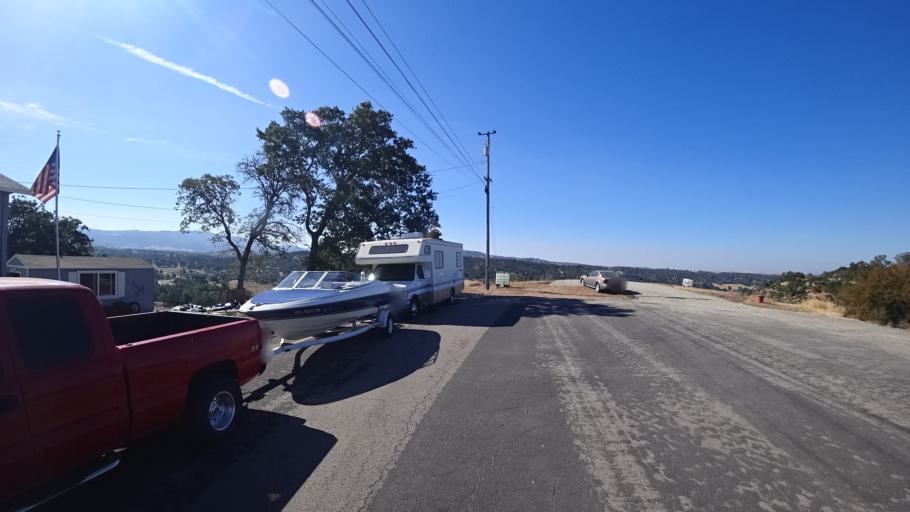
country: US
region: California
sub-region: Calaveras County
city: Rancho Calaveras
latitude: 38.1614
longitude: -120.8559
